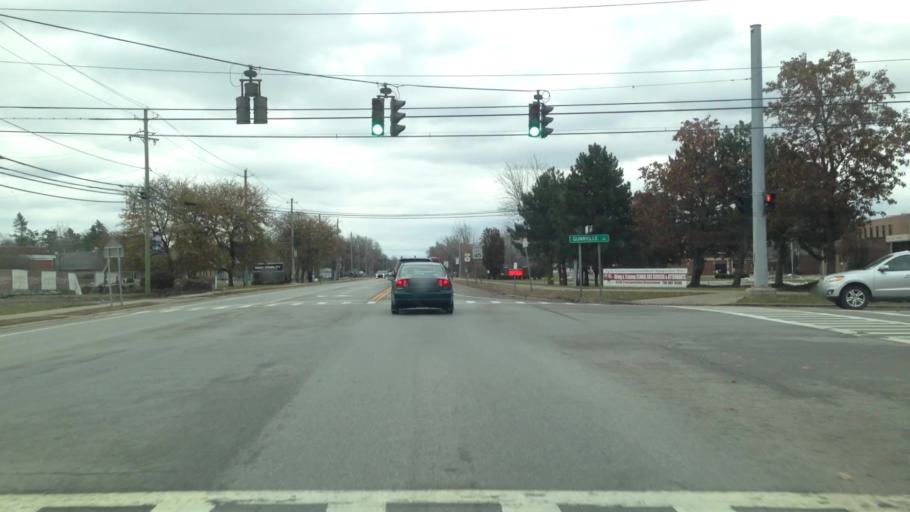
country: US
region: New York
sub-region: Erie County
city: Clarence Center
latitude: 42.9726
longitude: -78.6341
